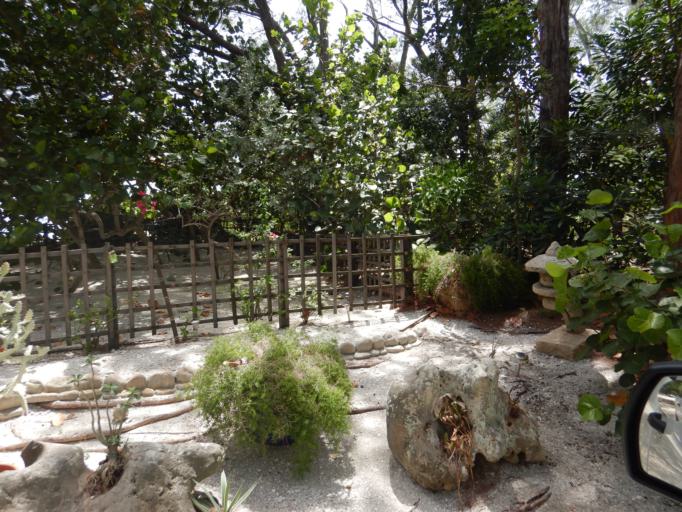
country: US
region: Florida
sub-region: Sarasota County
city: Gulf Gate Estates
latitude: 27.2288
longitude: -82.5218
